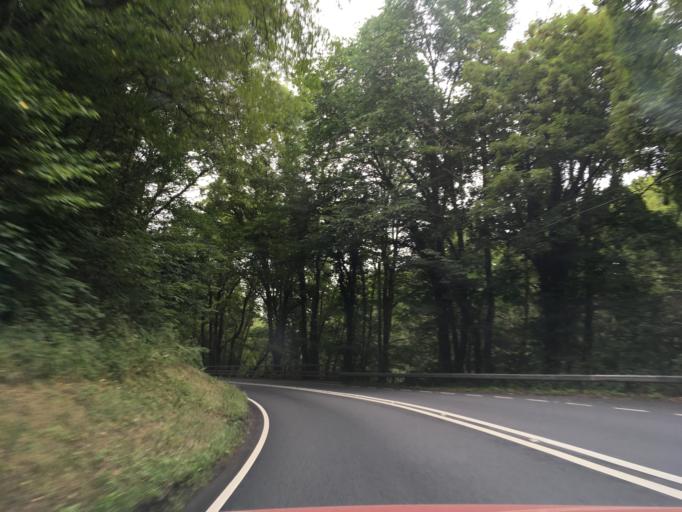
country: GB
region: Wales
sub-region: Carmarthenshire
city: Llandovery
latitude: 51.9962
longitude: -3.7415
